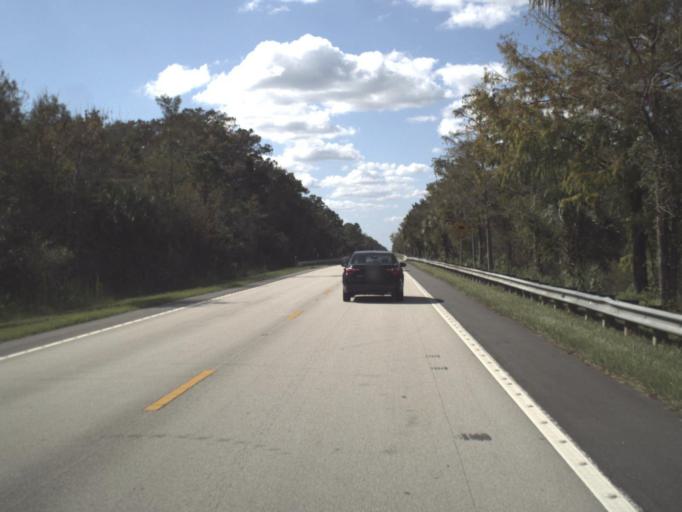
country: US
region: Florida
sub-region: Collier County
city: Marco
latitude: 25.8805
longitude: -81.2457
